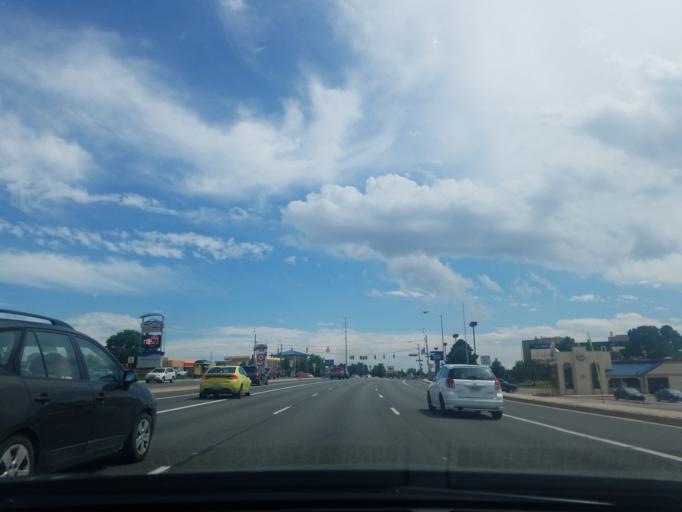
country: US
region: Colorado
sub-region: El Paso County
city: Air Force Academy
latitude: 38.9461
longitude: -104.8015
